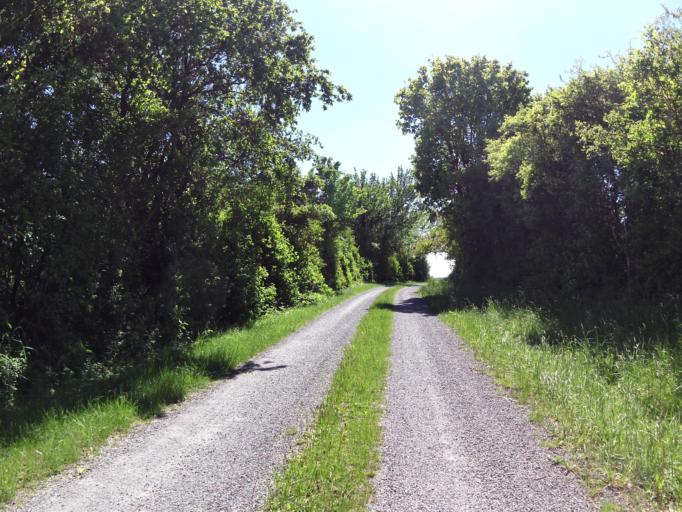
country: DE
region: Bavaria
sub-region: Regierungsbezirk Unterfranken
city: Reichenberg
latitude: 49.7502
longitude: 9.9323
